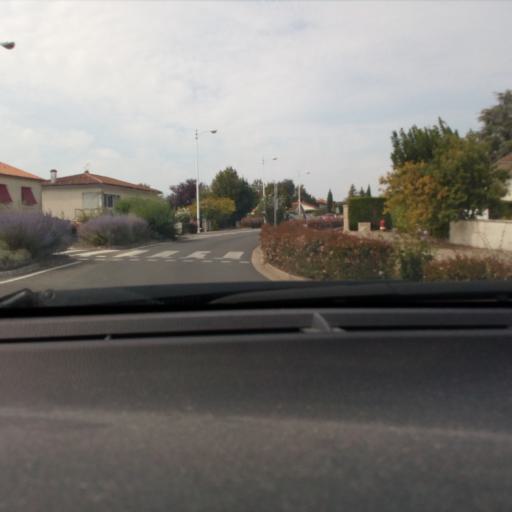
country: FR
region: Poitou-Charentes
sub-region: Departement de la Charente
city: Saint-Yrieix-sur-Charente
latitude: 45.6741
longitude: 0.1248
